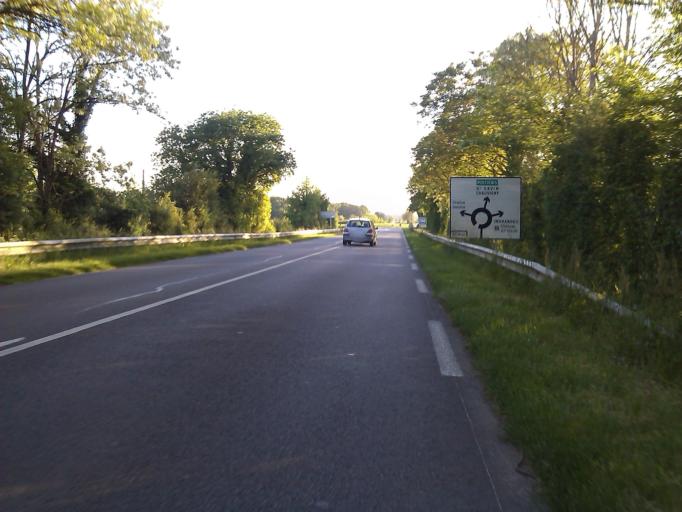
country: FR
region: Centre
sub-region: Departement de l'Indre
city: Le Blanc
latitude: 46.6034
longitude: 0.9821
